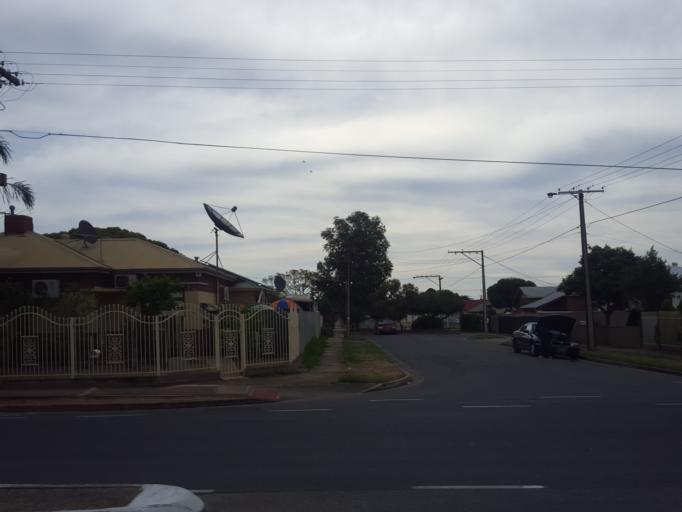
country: AU
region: South Australia
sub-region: Charles Sturt
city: Woodville North
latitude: -34.8666
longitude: 138.5478
